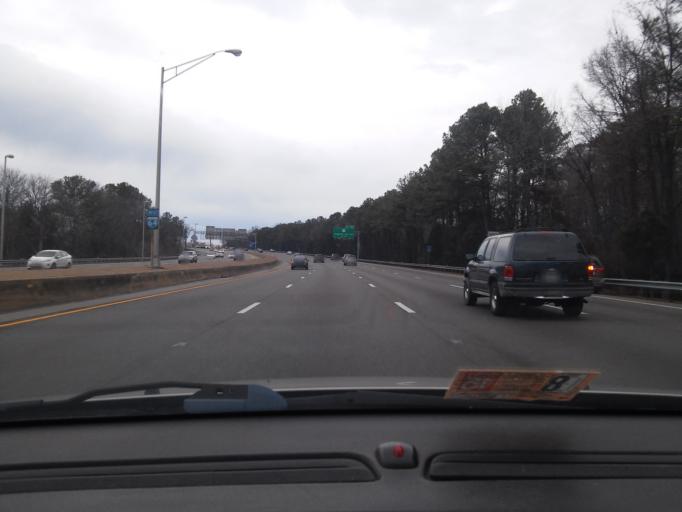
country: US
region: Virginia
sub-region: Henrico County
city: Lakeside
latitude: 37.5908
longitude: -77.4799
